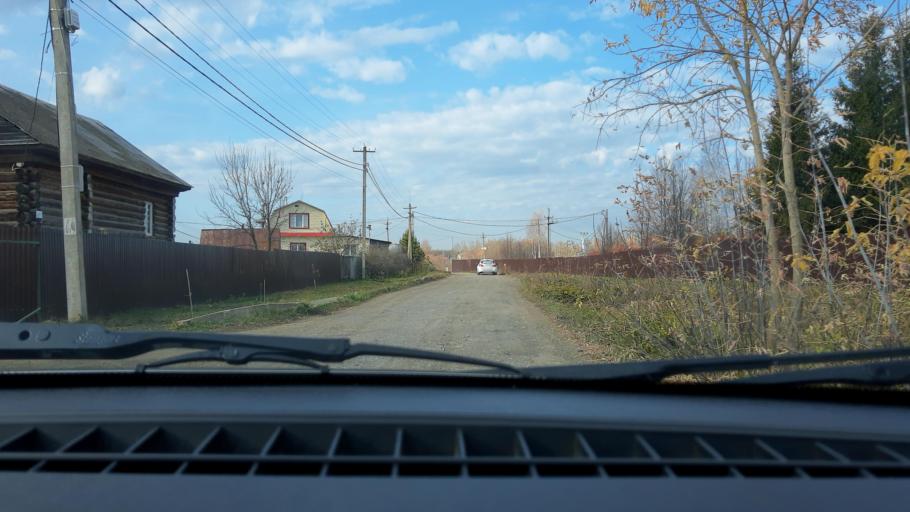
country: RU
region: Bashkortostan
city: Ufa
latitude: 54.6654
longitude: 55.9264
